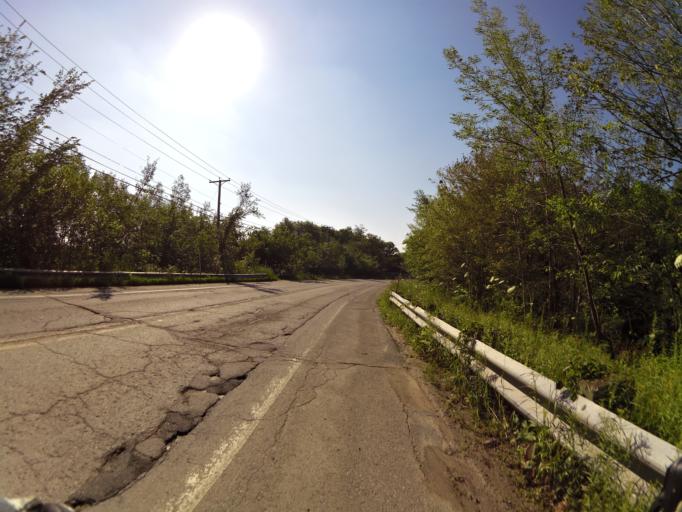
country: CA
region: Quebec
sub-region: Outaouais
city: Gatineau
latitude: 45.5235
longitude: -75.7913
